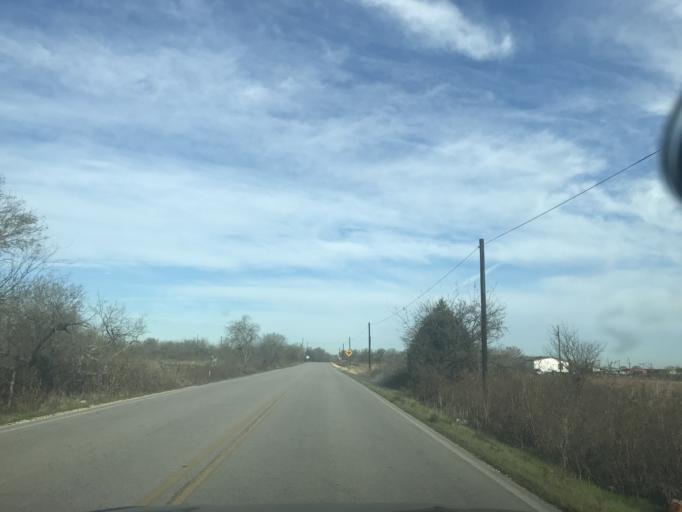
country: US
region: Texas
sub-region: Travis County
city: Manor
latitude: 30.2983
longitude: -97.5269
